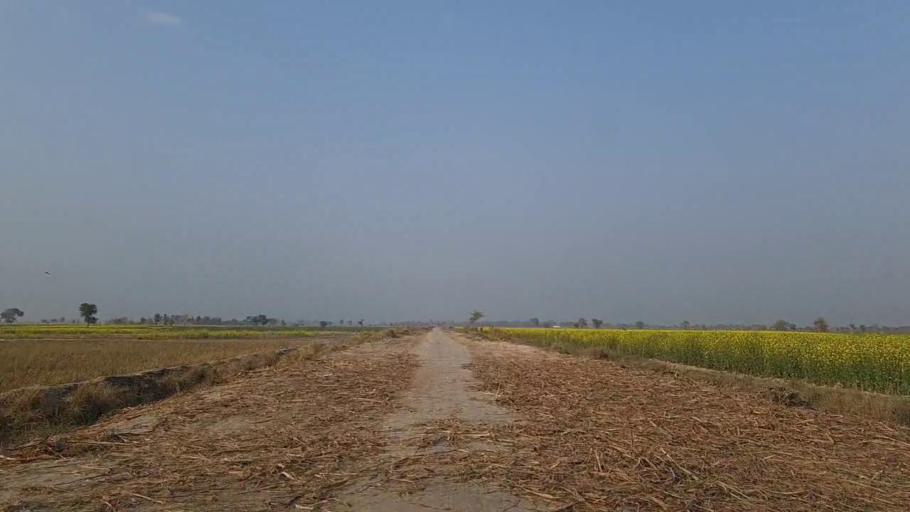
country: PK
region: Sindh
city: Jam Sahib
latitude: 26.3359
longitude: 68.5148
